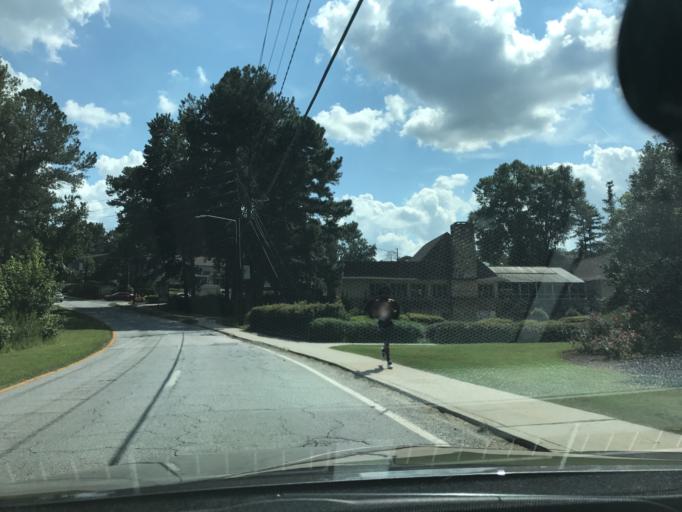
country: US
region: Georgia
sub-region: DeKalb County
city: Clarkston
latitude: 33.7934
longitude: -84.2140
